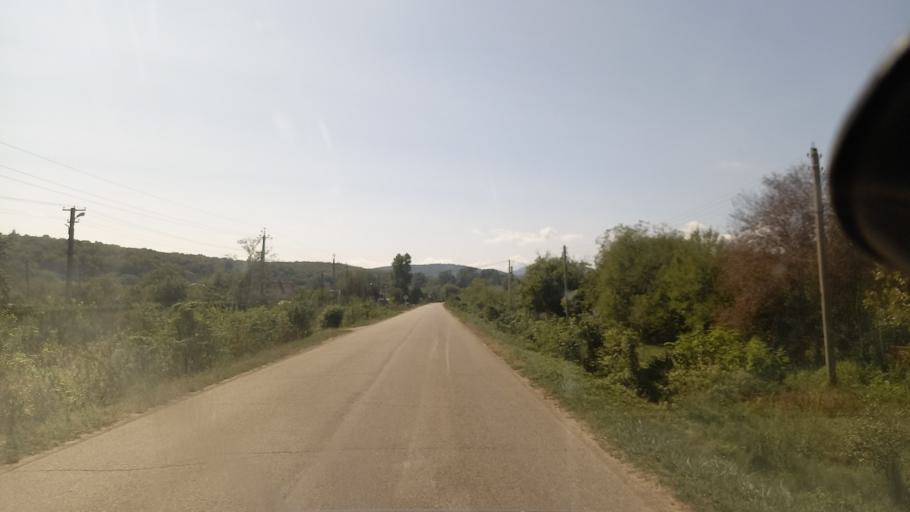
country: RU
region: Krasnodarskiy
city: Azovskaya
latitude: 44.7112
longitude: 38.6866
